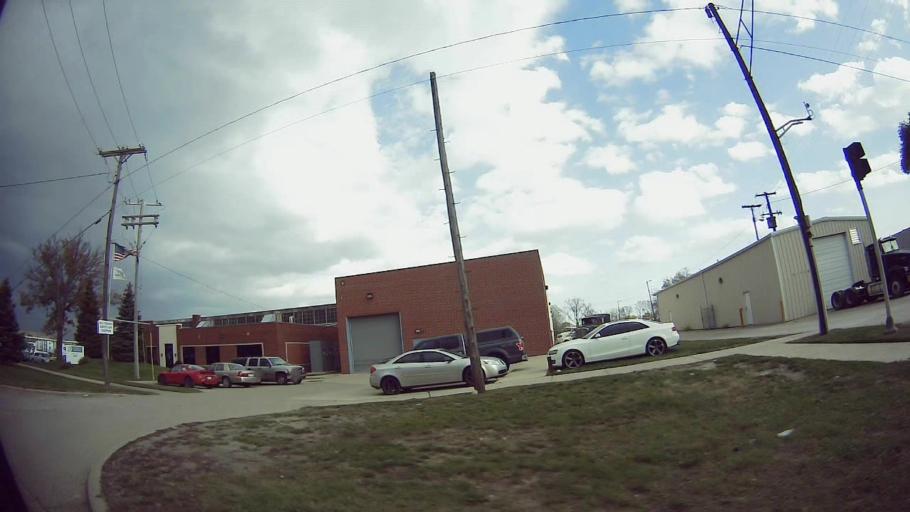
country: US
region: Michigan
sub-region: Macomb County
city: Warren
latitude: 42.4546
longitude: -83.0053
